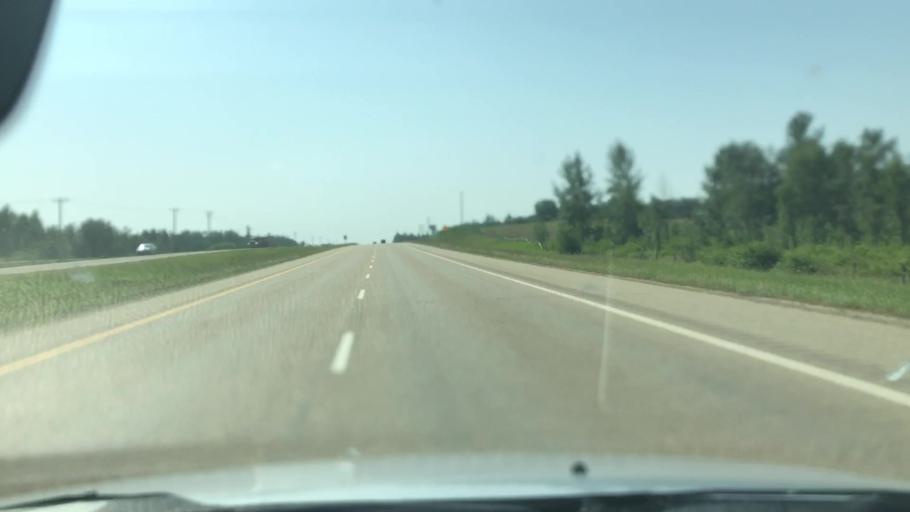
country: CA
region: Alberta
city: Devon
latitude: 53.4423
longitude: -113.7632
